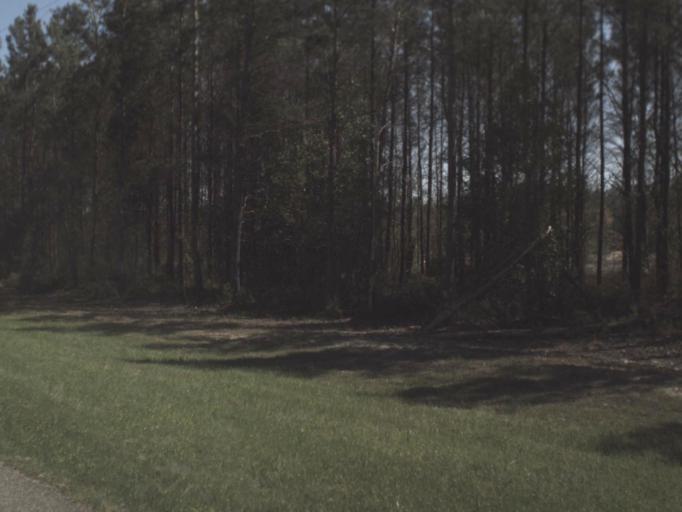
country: US
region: Florida
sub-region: Liberty County
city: Bristol
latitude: 30.4103
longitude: -84.8461
